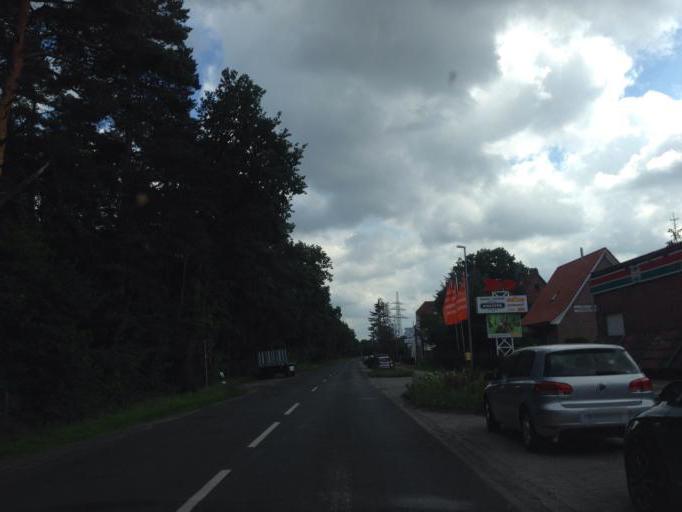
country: DE
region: Lower Saxony
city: Adendorf
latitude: 53.2981
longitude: 10.4288
